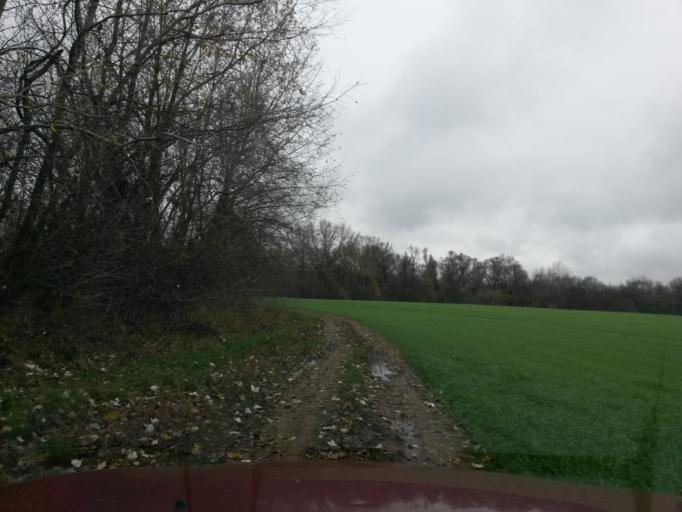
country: SK
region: Kosicky
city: Michalovce
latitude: 48.5624
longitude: 21.9397
